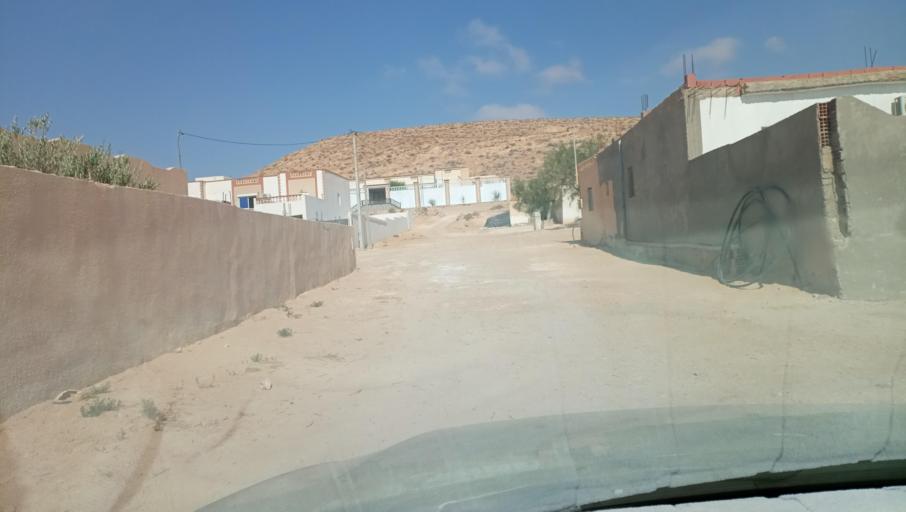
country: TN
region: Tataouine
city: Tataouine
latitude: 32.9853
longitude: 10.3854
